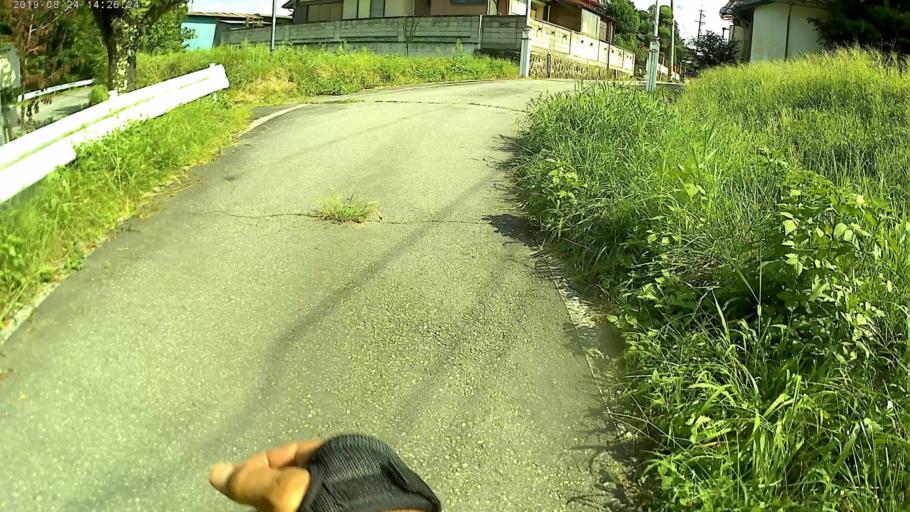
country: JP
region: Nagano
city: Komoro
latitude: 36.2689
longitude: 138.4317
